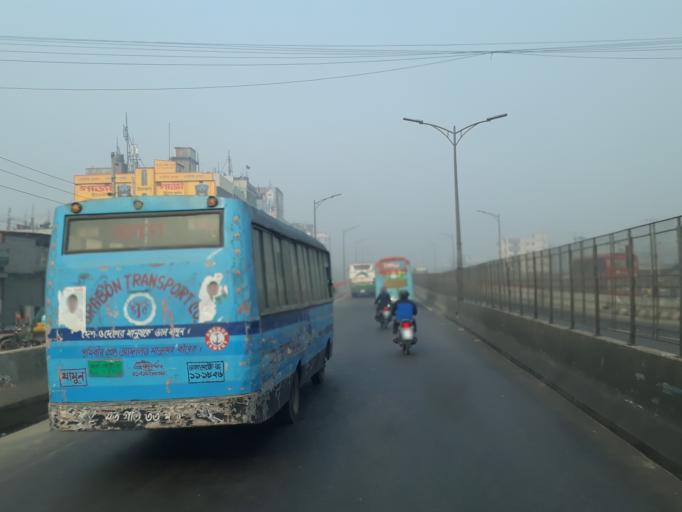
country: BD
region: Dhaka
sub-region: Dhaka
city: Dhaka
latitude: 23.7076
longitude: 90.4398
